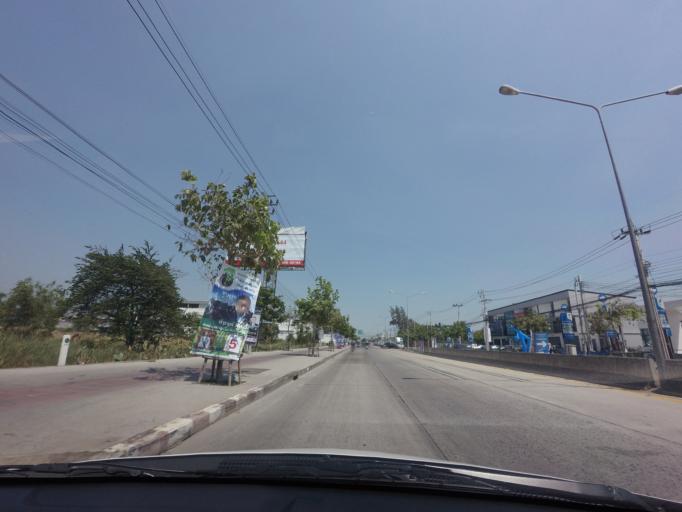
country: TH
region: Bangkok
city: Nong Chok
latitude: 13.8558
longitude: 100.8521
